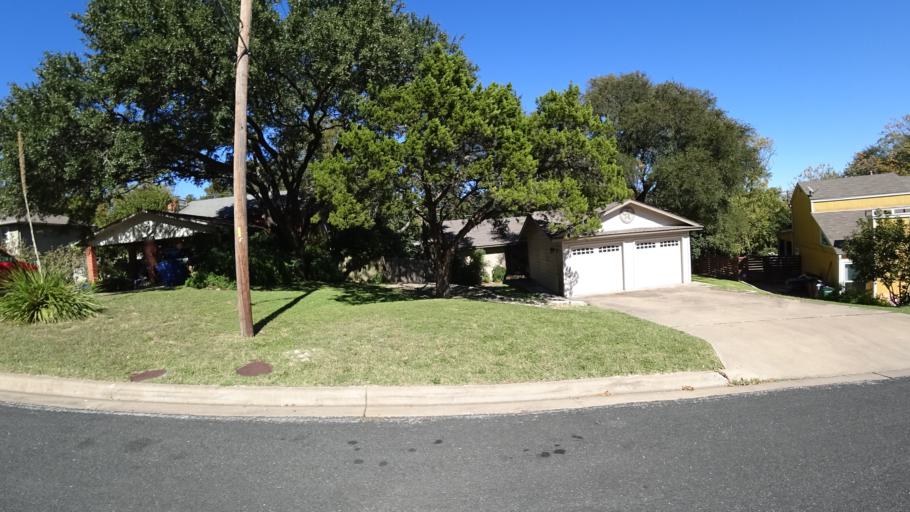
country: US
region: Texas
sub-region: Travis County
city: Rollingwood
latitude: 30.2344
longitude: -97.7794
